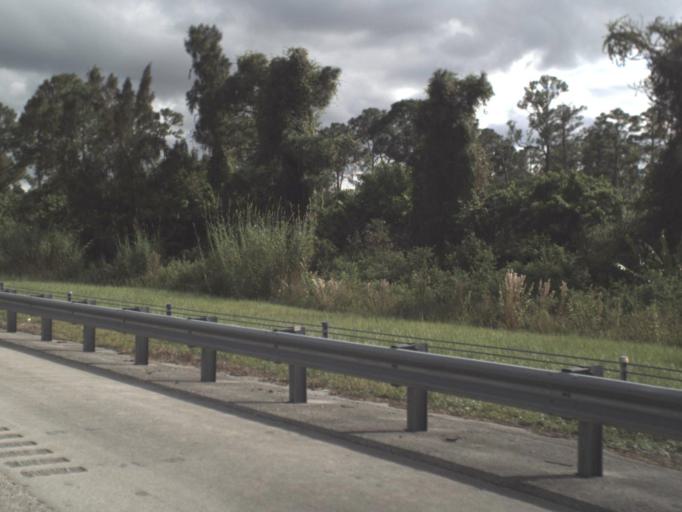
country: US
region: Florida
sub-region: Martin County
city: Palm City
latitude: 27.1062
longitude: -80.2666
